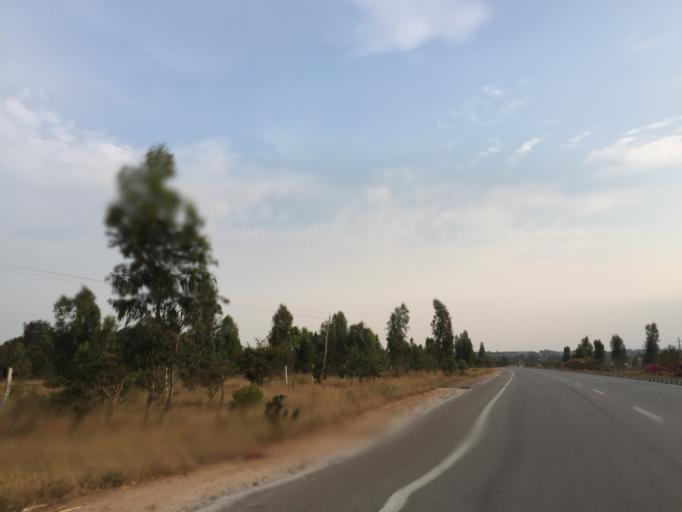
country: IN
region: Karnataka
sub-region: Chikkaballapur
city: Chik Ballapur
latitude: 13.4026
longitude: 77.7425
